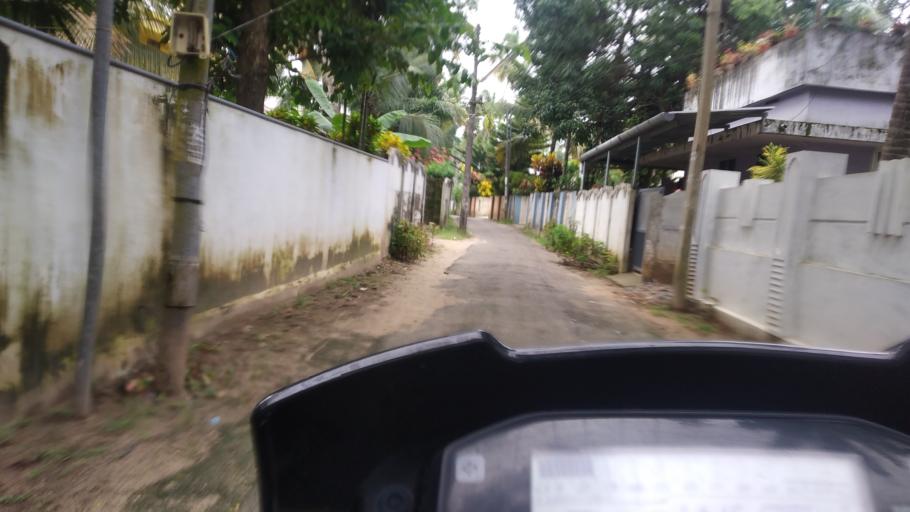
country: IN
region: Kerala
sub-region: Ernakulam
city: Elur
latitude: 10.0627
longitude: 76.2168
